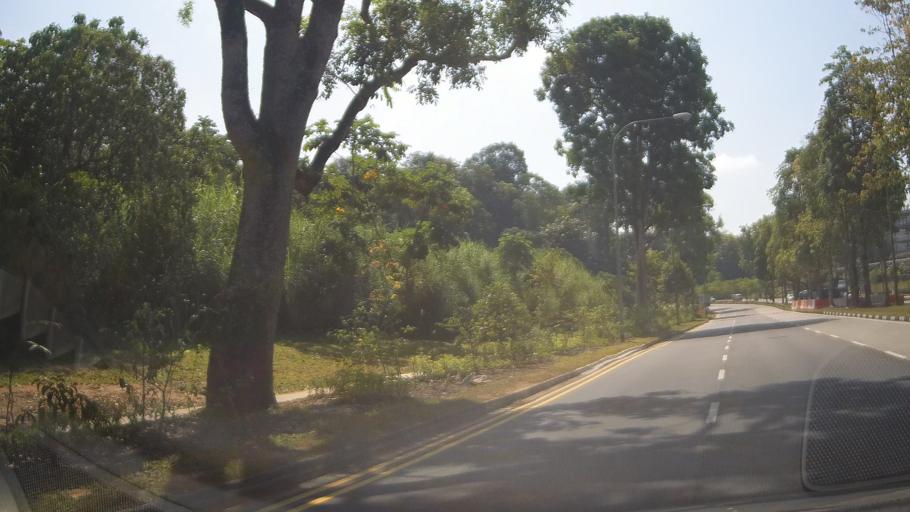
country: MY
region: Johor
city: Johor Bahru
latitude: 1.4113
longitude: 103.7618
